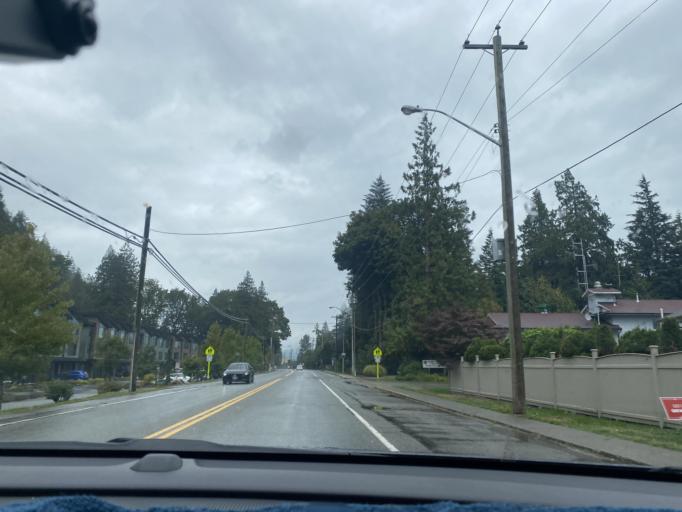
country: CA
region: British Columbia
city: Agassiz
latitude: 49.2964
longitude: -121.7842
